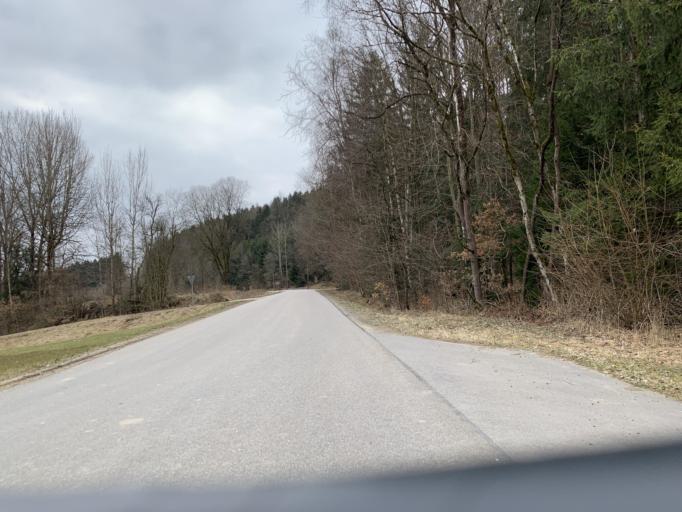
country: DE
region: Bavaria
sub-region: Upper Palatinate
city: Thanstein
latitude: 49.3831
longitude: 12.4508
